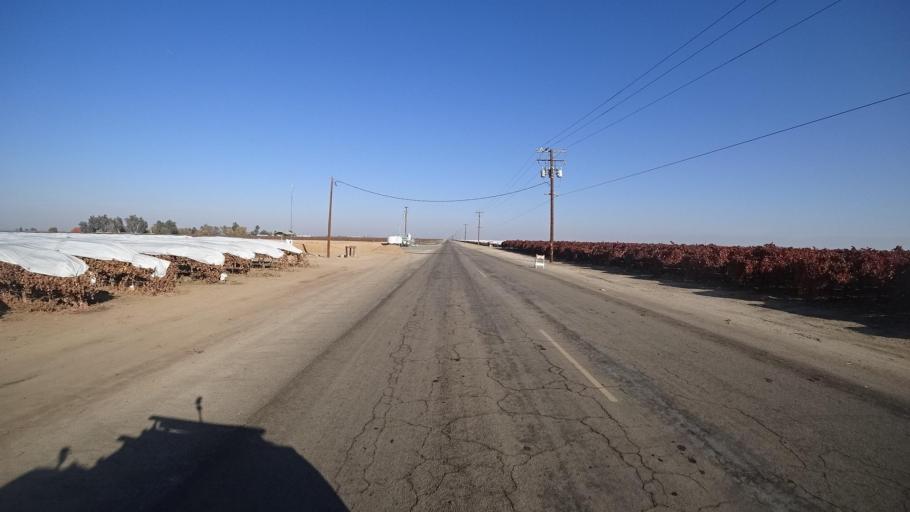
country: US
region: California
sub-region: Kern County
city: Delano
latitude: 35.7390
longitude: -119.1695
